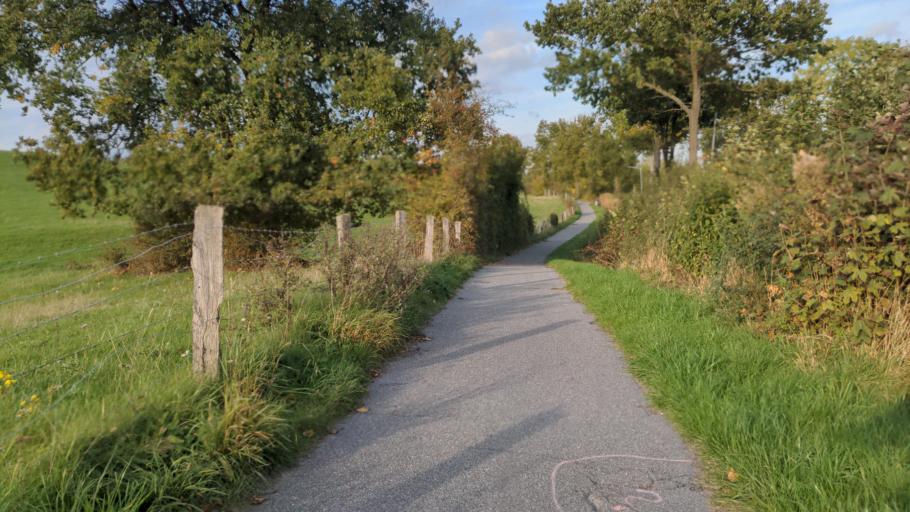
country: DE
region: Schleswig-Holstein
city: Ahrensbok
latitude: 54.0038
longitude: 10.5823
